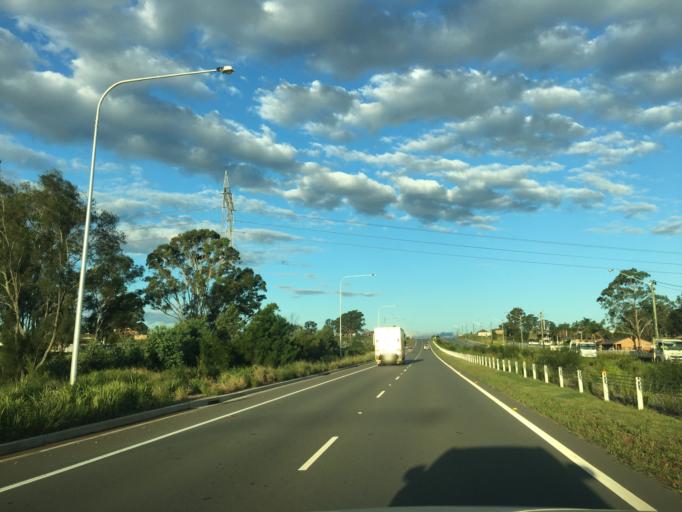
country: AU
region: New South Wales
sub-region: Liverpool
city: Bringelly
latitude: -33.9479
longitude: 150.7894
